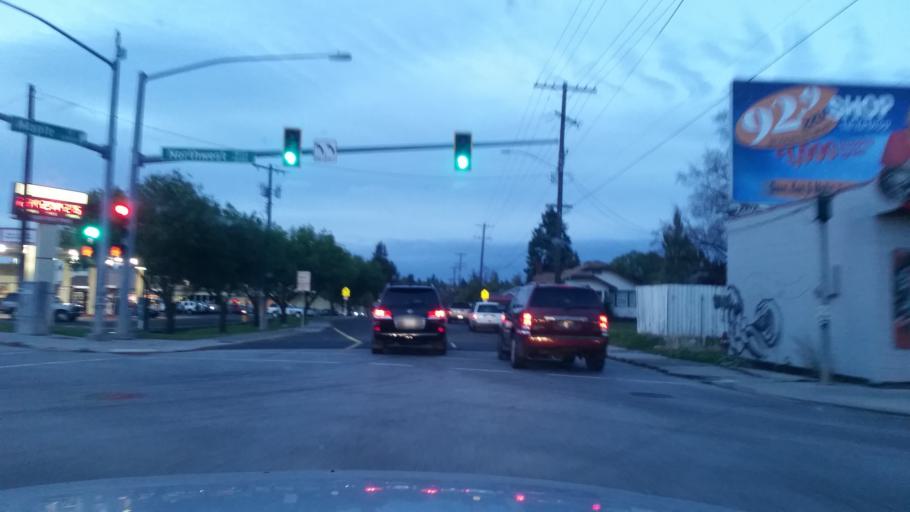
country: US
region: Washington
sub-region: Spokane County
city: Spokane
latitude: 47.6790
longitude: -117.4355
